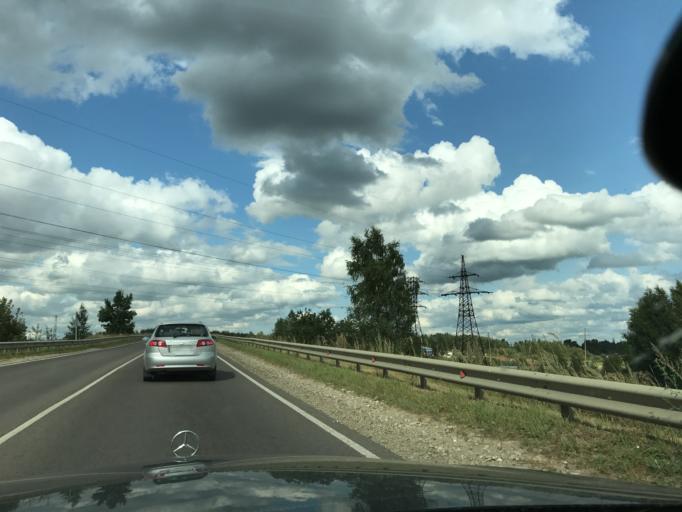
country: RU
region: Vladimir
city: Sobinka
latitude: 56.0175
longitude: 39.9926
